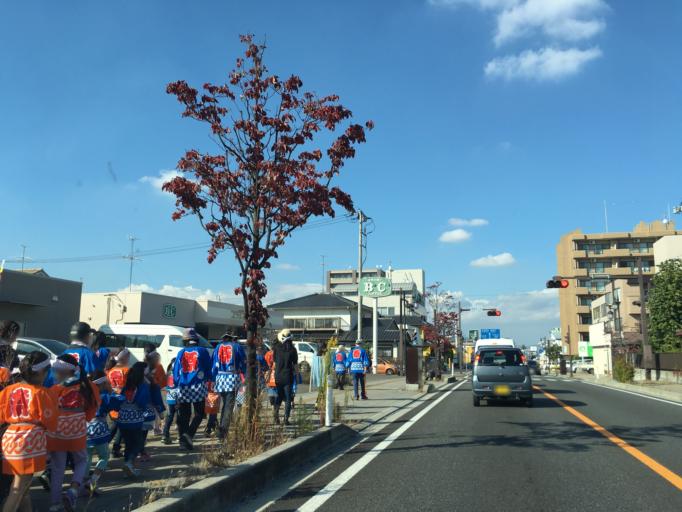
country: JP
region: Fukushima
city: Koriyama
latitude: 37.3894
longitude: 140.3552
